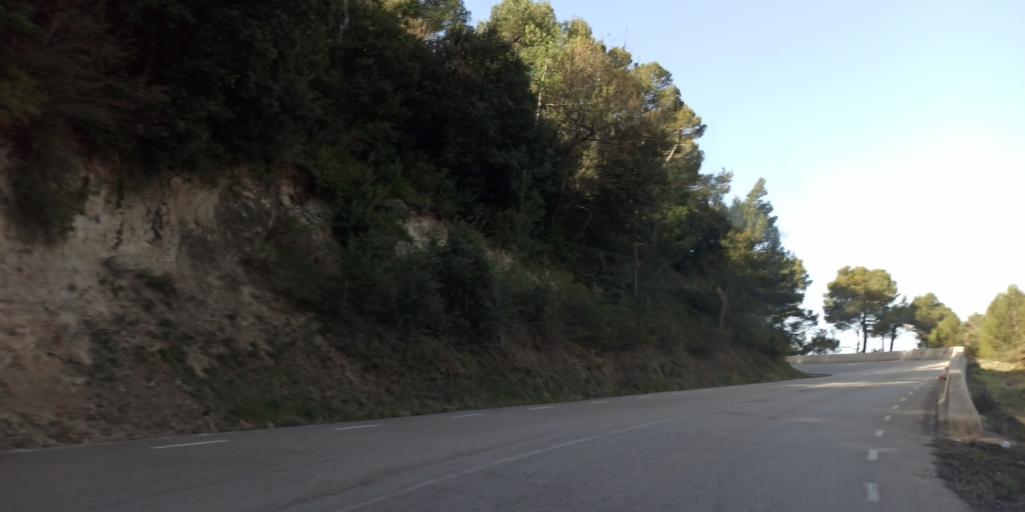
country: ES
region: Catalonia
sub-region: Provincia de Barcelona
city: Castelloli
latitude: 41.5970
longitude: 1.7239
